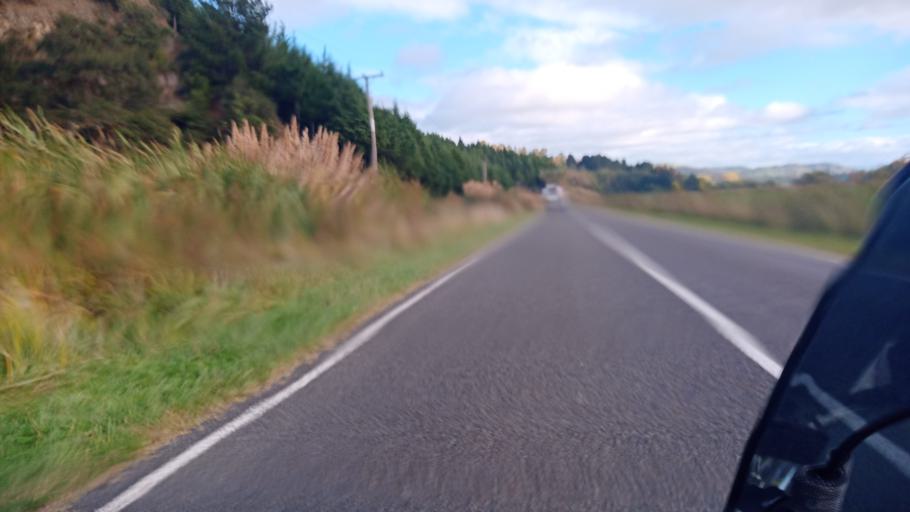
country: NZ
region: Gisborne
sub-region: Gisborne District
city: Gisborne
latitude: -38.6049
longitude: 177.8088
